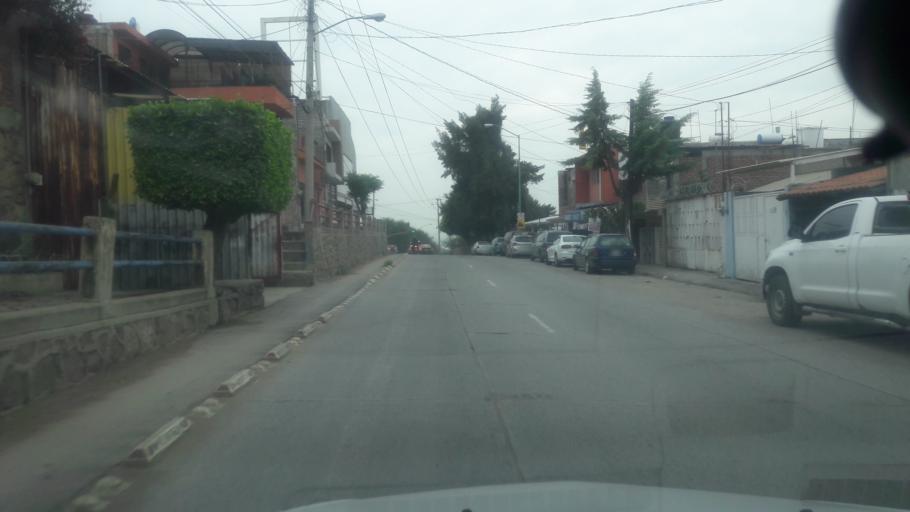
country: MX
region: Guanajuato
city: Leon
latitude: 21.1255
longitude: -101.7059
